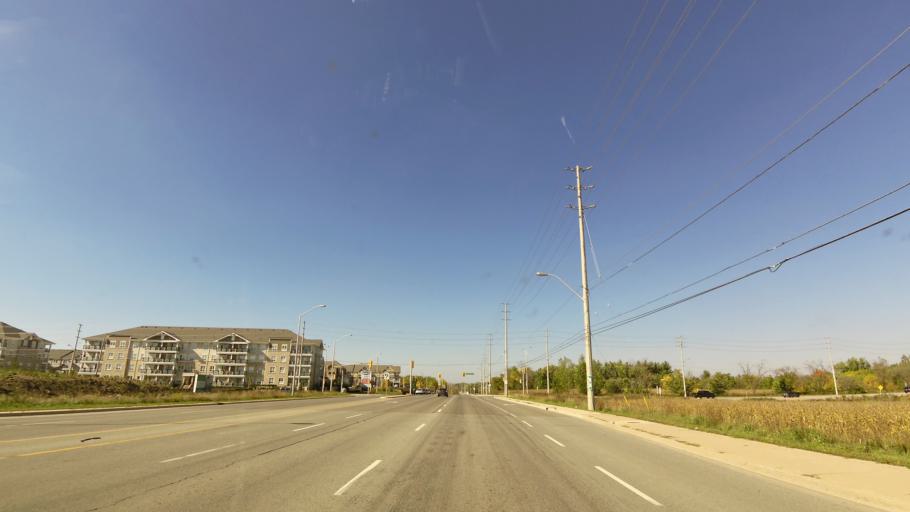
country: CA
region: Ontario
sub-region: Halton
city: Milton
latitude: 43.4959
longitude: -79.8471
